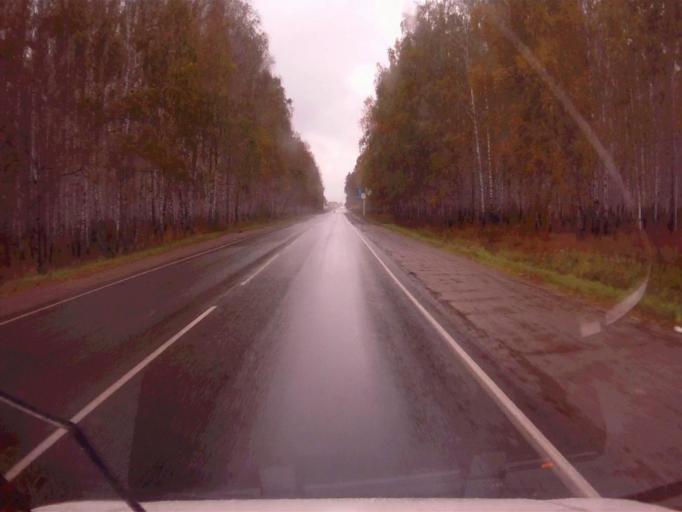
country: RU
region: Chelyabinsk
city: Argayash
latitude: 55.4136
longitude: 61.0353
